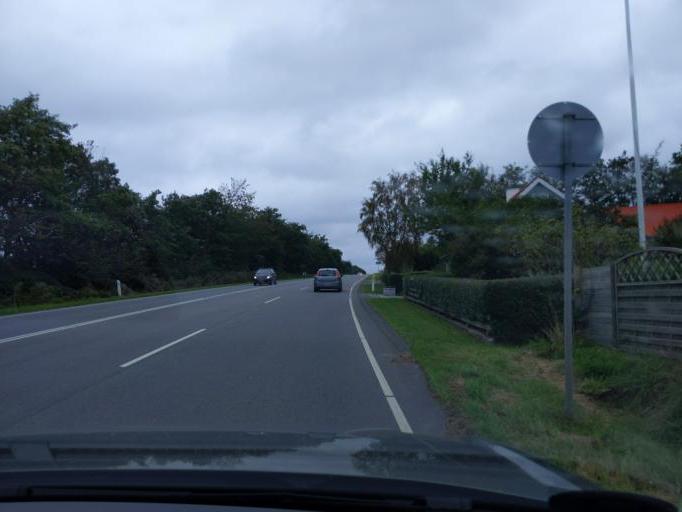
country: DK
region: North Denmark
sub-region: Mariagerfjord Kommune
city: Hobro
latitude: 56.5712
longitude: 9.8182
